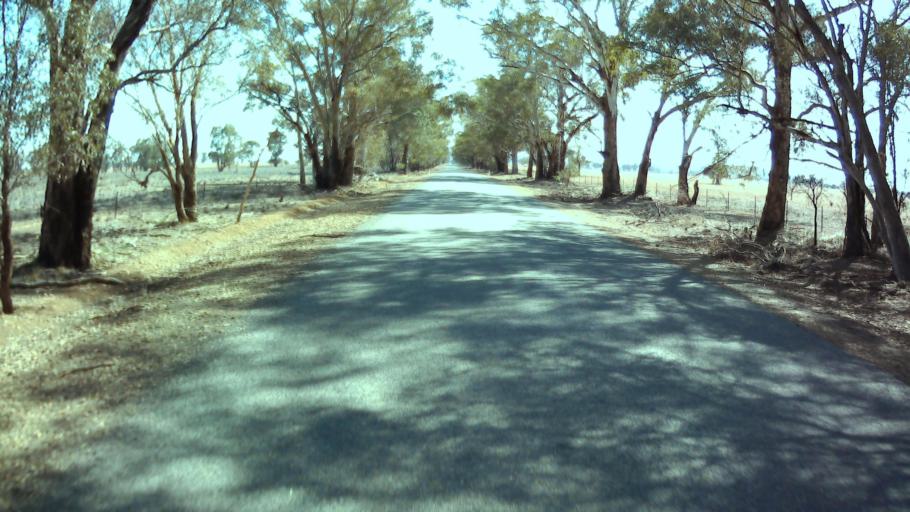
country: AU
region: New South Wales
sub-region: Weddin
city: Grenfell
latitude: -33.7240
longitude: 147.8960
